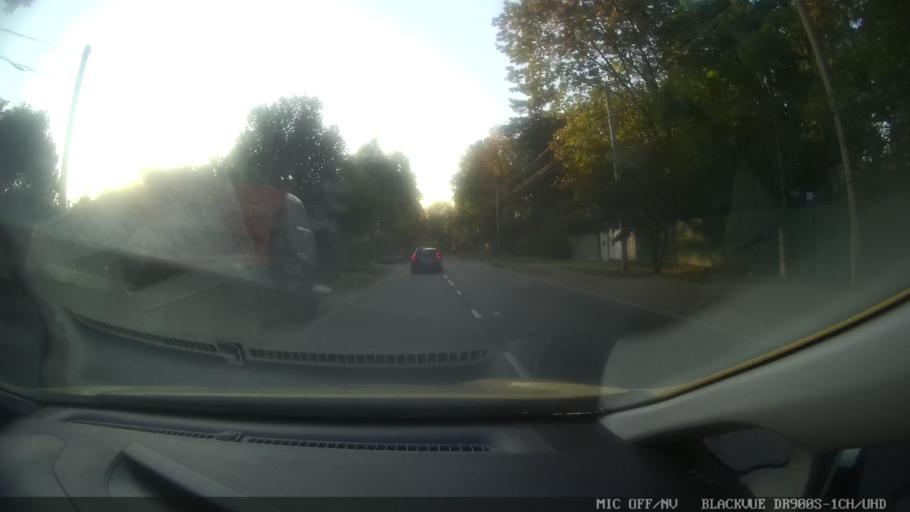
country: RU
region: Moscow
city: Zhulebino
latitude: 55.7012
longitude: 37.8636
